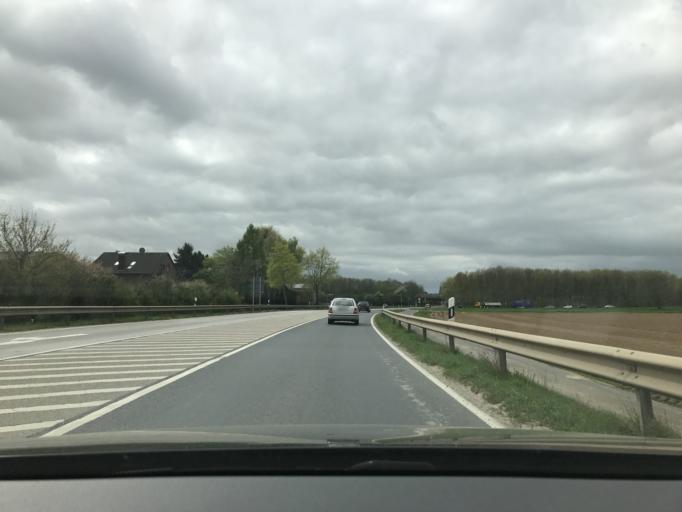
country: DE
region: North Rhine-Westphalia
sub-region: Regierungsbezirk Dusseldorf
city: Kaarst
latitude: 51.2407
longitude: 6.6218
